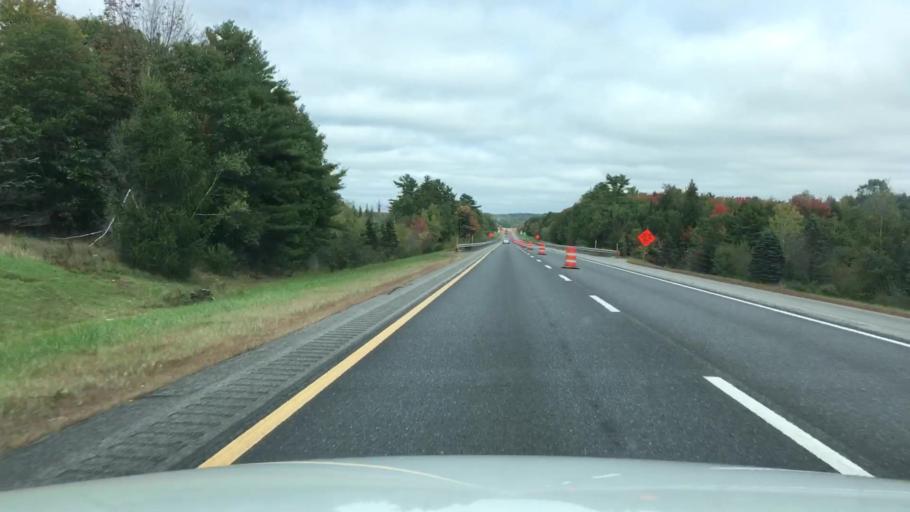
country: US
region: Maine
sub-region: Sagadahoc County
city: Richmond
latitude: 44.1324
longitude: -69.8455
